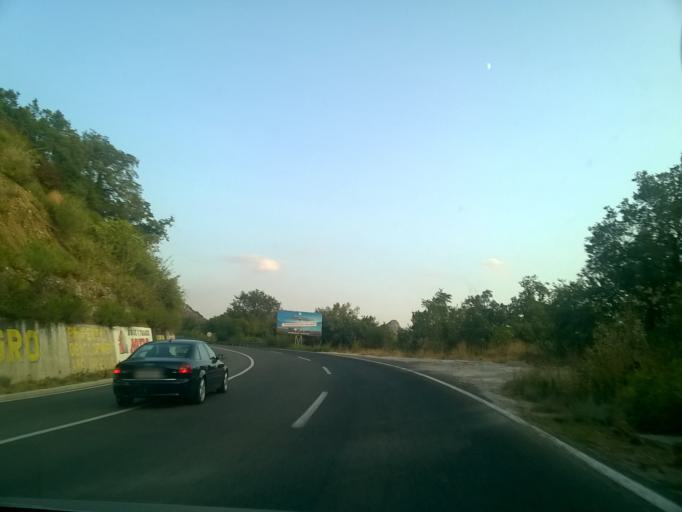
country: ME
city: Petrovac na Moru
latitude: 42.1948
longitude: 18.9830
